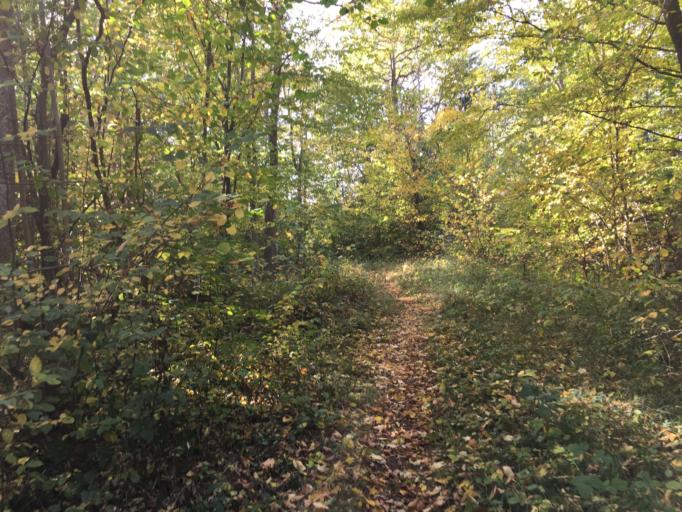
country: SE
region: Kalmar
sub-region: Borgholms Kommun
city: Borgholm
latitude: 56.7478
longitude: 16.6147
